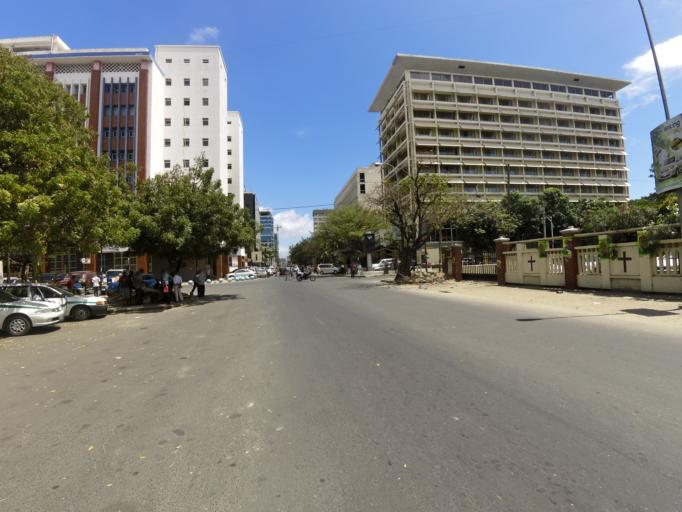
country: TZ
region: Dar es Salaam
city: Dar es Salaam
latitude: -6.8179
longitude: 39.2907
